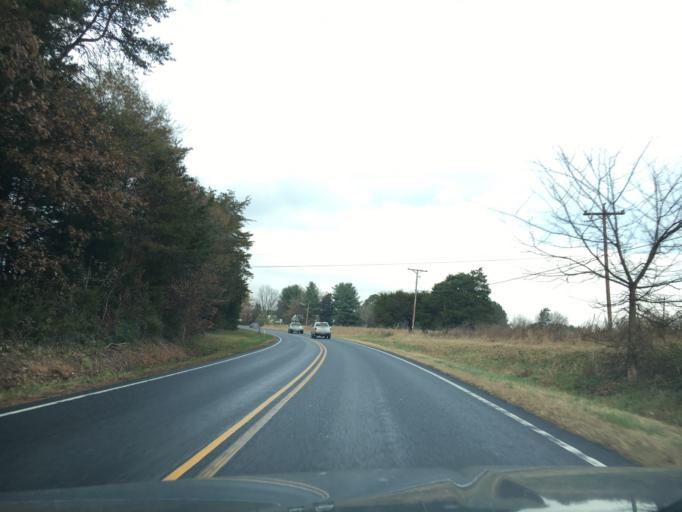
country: US
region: Virginia
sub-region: Prince Edward County
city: Farmville
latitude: 37.3309
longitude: -78.3859
